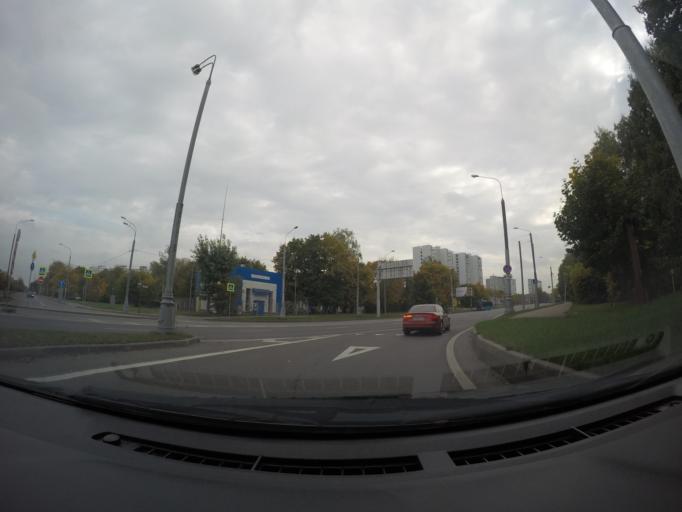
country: RU
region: Moscow
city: Ivanovskoye
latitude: 55.7711
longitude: 37.8198
